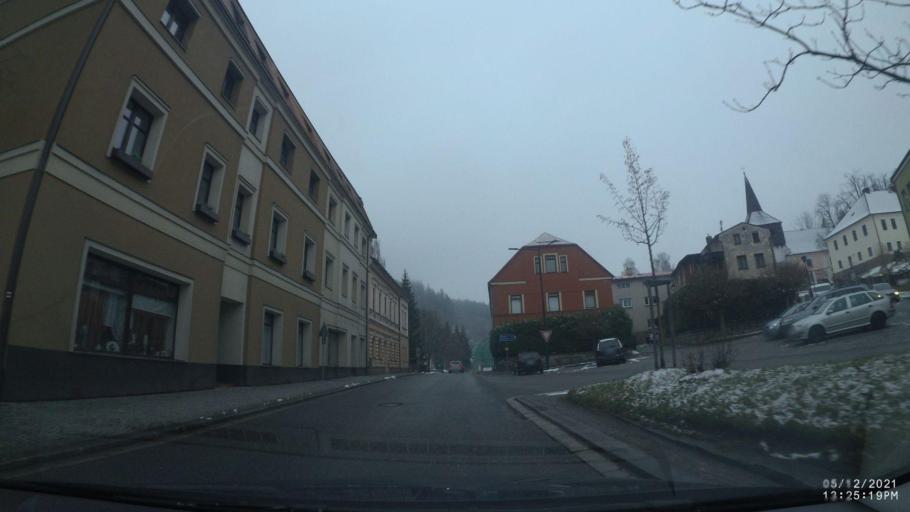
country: CZ
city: Hronov
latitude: 50.4820
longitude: 16.1816
